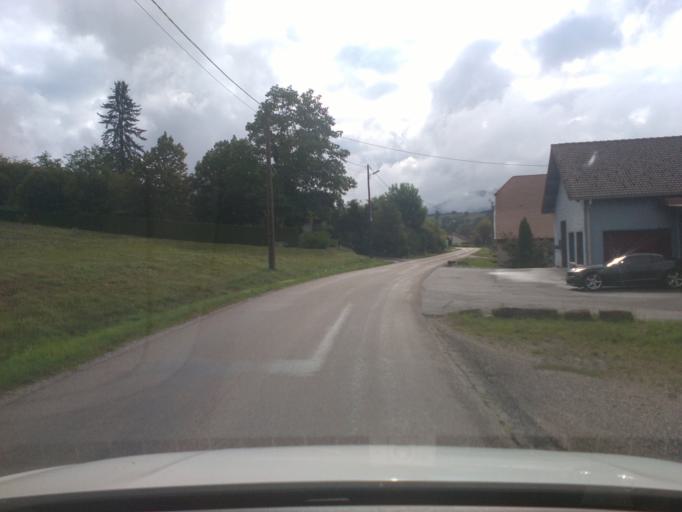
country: FR
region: Lorraine
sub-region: Departement des Vosges
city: Senones
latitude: 48.3459
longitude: 6.9554
